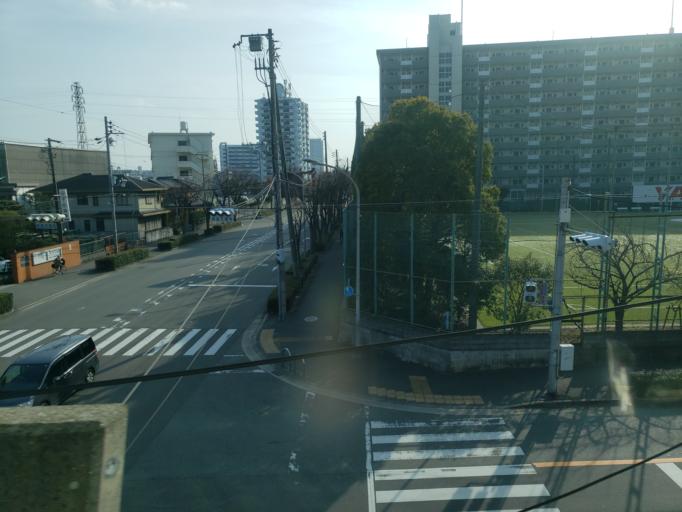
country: JP
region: Hyogo
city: Amagasaki
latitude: 34.7301
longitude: 135.4408
